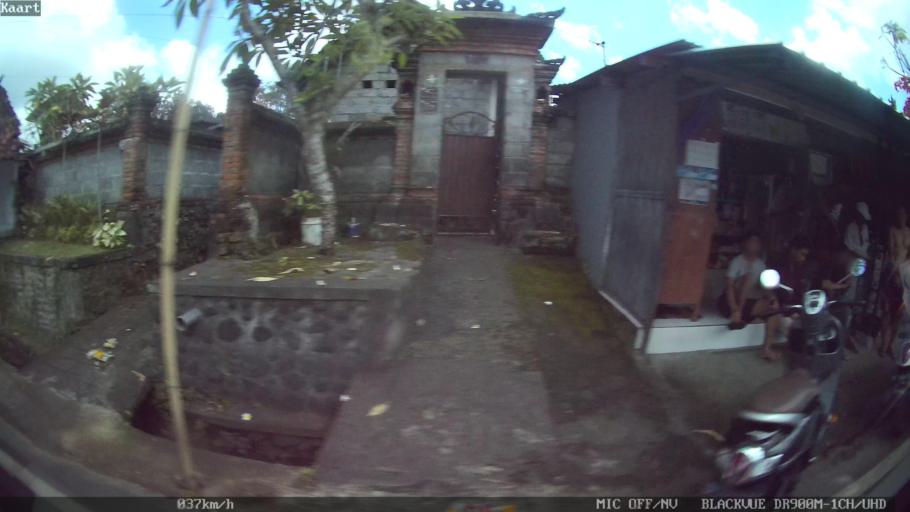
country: ID
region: Bali
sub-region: Kabupaten Gianyar
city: Ubud
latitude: -8.5410
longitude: 115.2805
